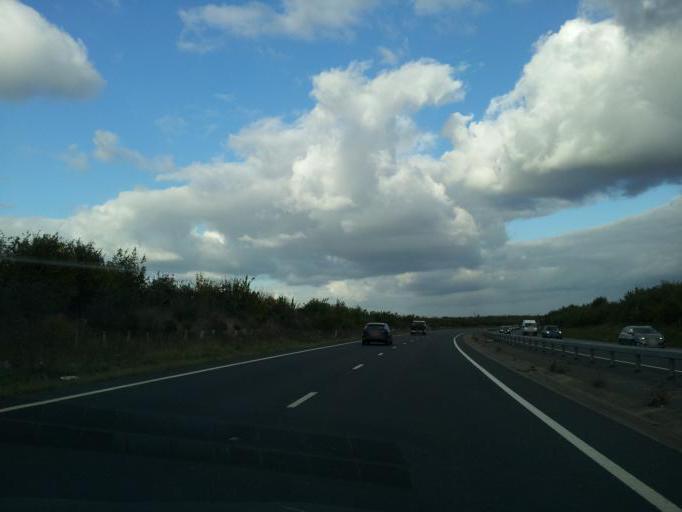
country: GB
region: England
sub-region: Bedford
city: Roxton
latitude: 52.1820
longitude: -0.3185
